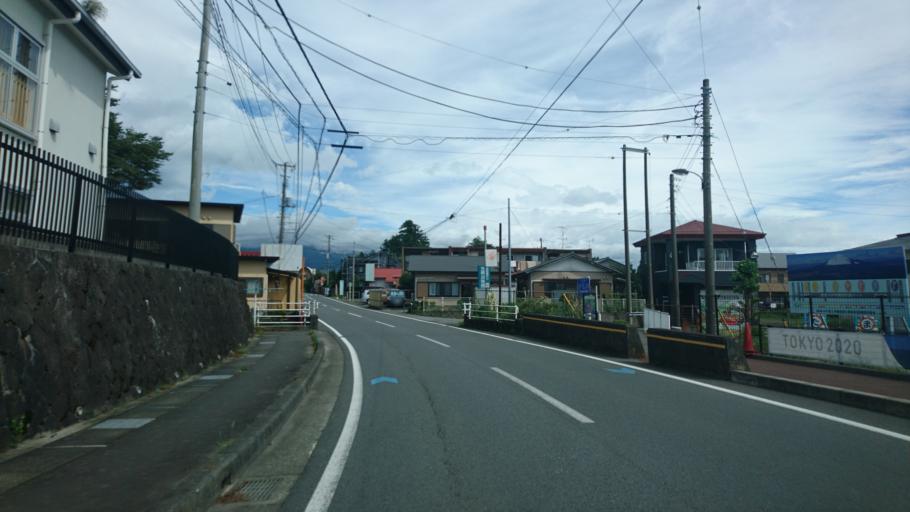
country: JP
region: Shizuoka
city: Gotemba
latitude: 35.3161
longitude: 138.9067
